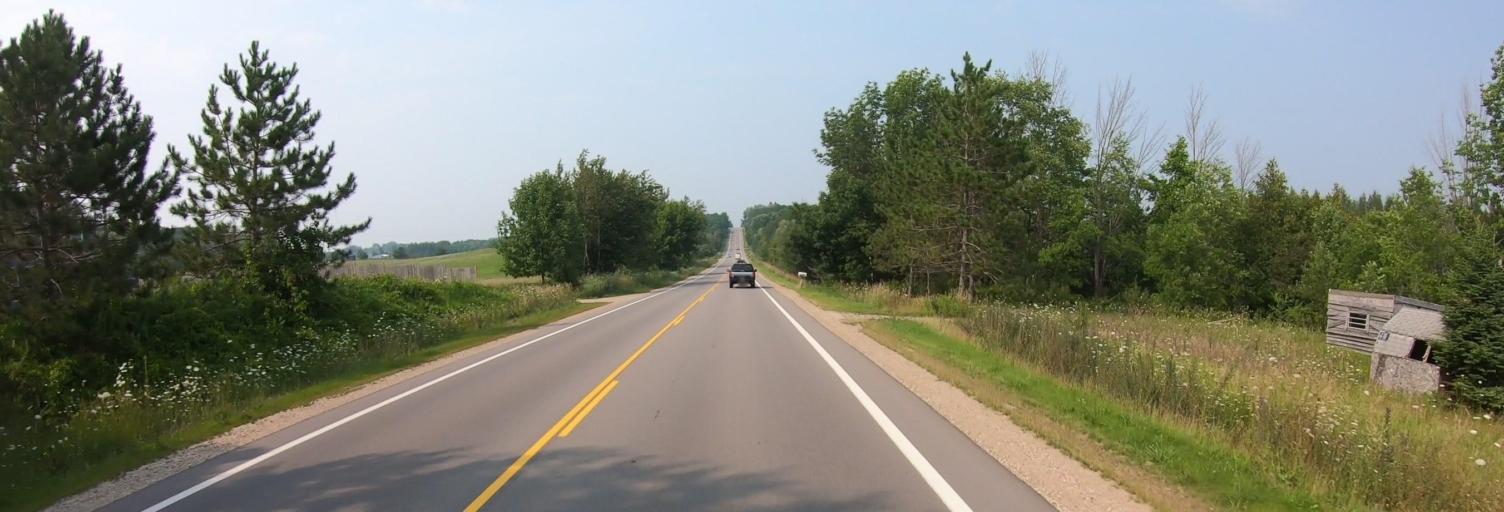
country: US
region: Michigan
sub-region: Charlevoix County
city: Charlevoix
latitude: 45.2353
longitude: -85.2613
